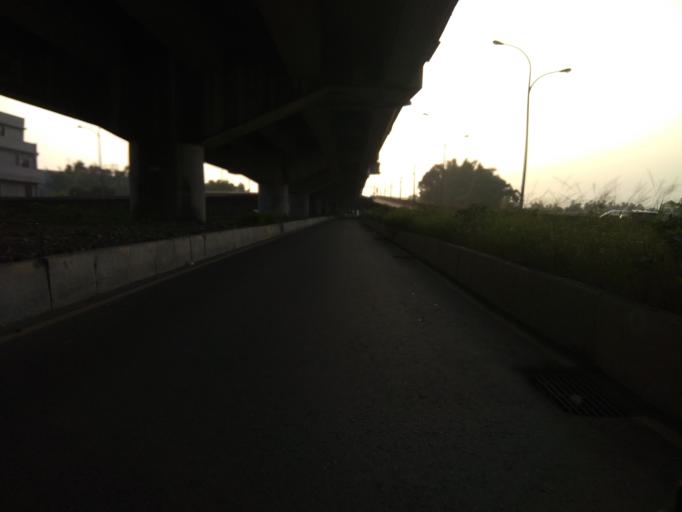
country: TW
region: Taiwan
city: Daxi
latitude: 24.9274
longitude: 121.2147
